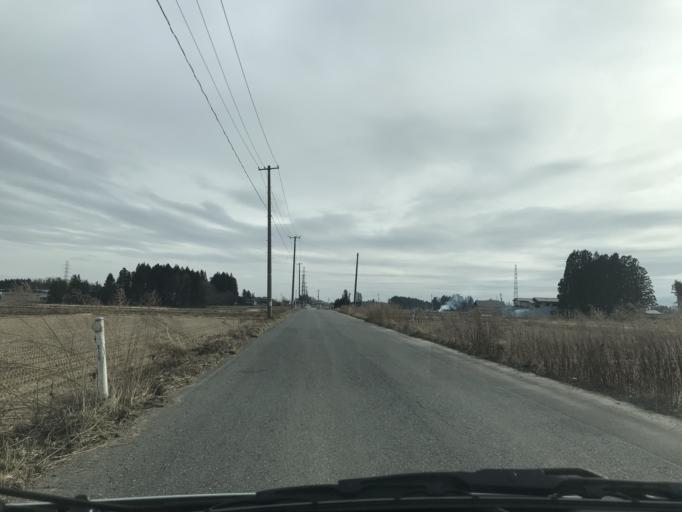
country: JP
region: Iwate
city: Hanamaki
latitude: 39.3440
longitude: 141.0598
